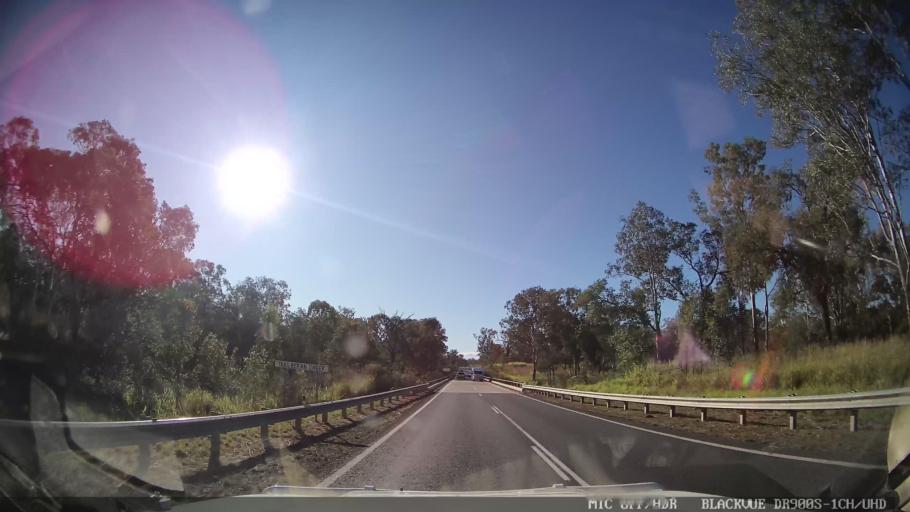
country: AU
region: Queensland
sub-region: Bundaberg
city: Sharon
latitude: -24.8288
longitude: 151.7082
